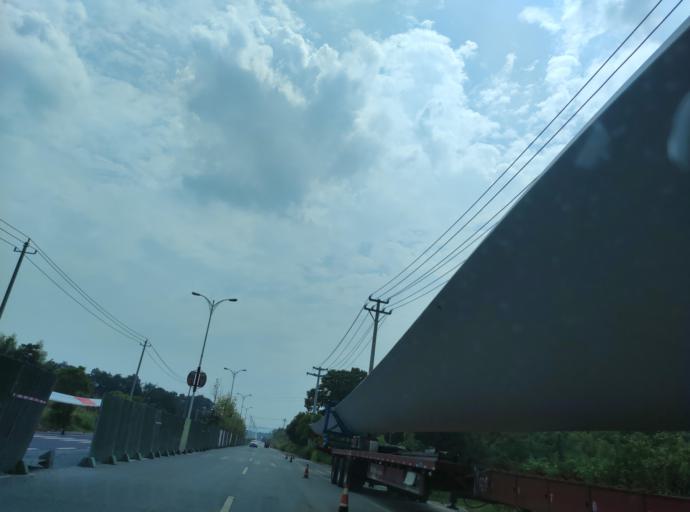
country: CN
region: Jiangxi Sheng
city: Yuannan
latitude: 27.6640
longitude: 114.0285
